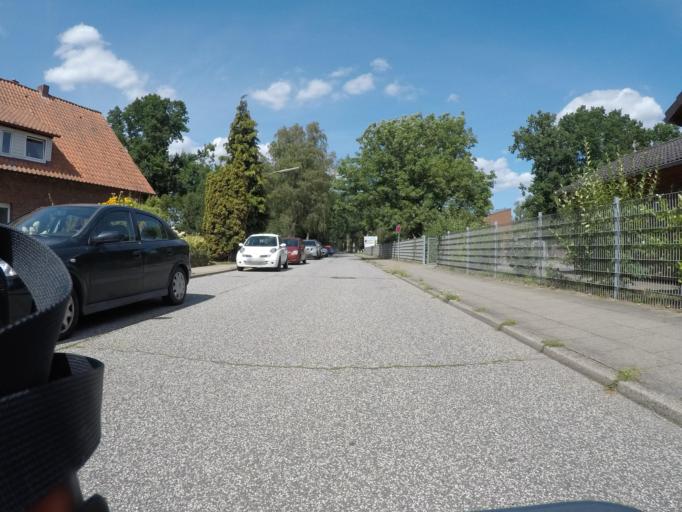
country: DE
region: Lower Saxony
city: Stelle
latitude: 53.4457
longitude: 10.1306
